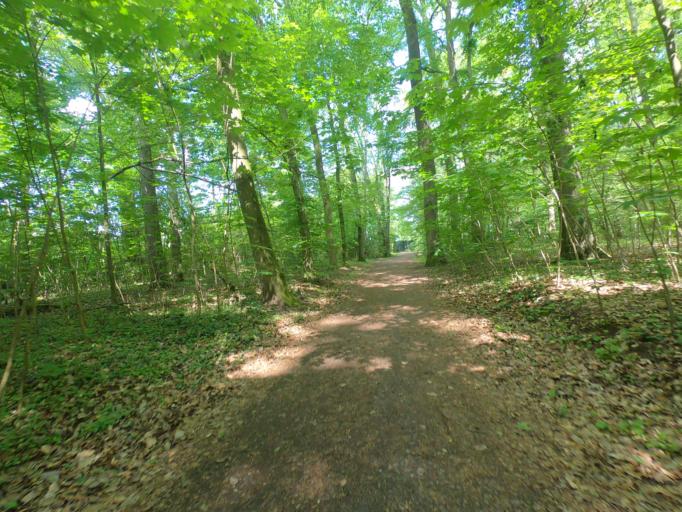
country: DE
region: Hesse
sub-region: Regierungsbezirk Darmstadt
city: Neu Isenburg
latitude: 50.0786
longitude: 8.6843
